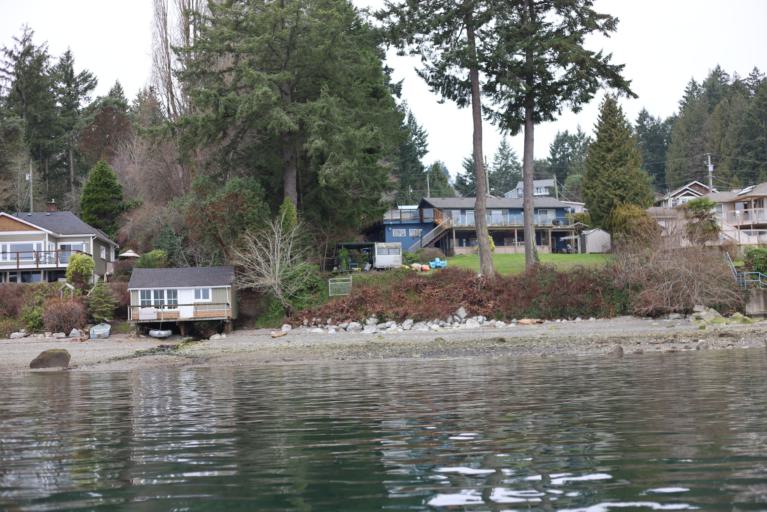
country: CA
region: British Columbia
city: North Saanich
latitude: 48.6412
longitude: -123.5409
